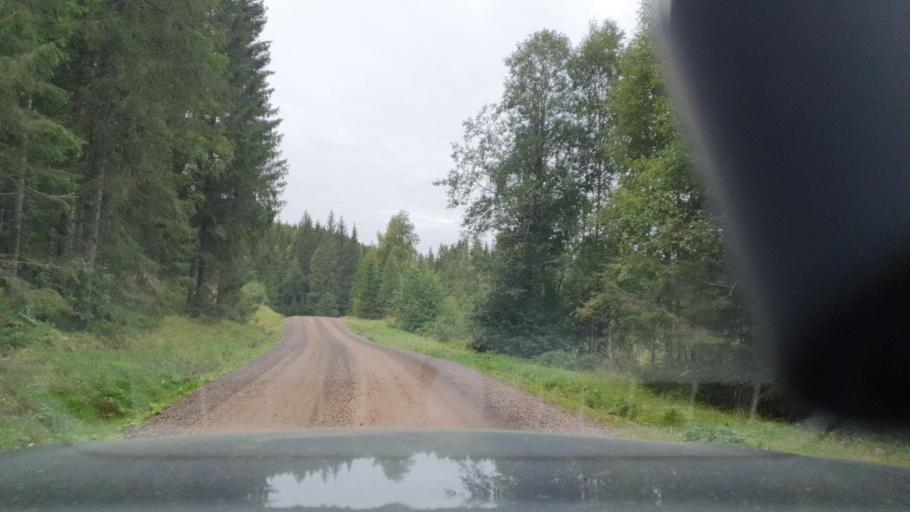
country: SE
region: Vaermland
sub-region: Eda Kommun
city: Charlottenberg
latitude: 60.0322
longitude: 12.6003
